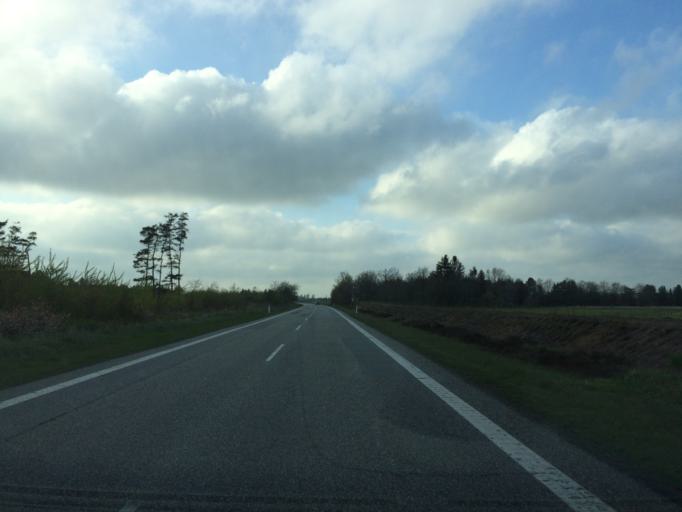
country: DK
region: Central Jutland
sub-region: Viborg Kommune
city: Karup
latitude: 56.3228
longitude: 9.1125
